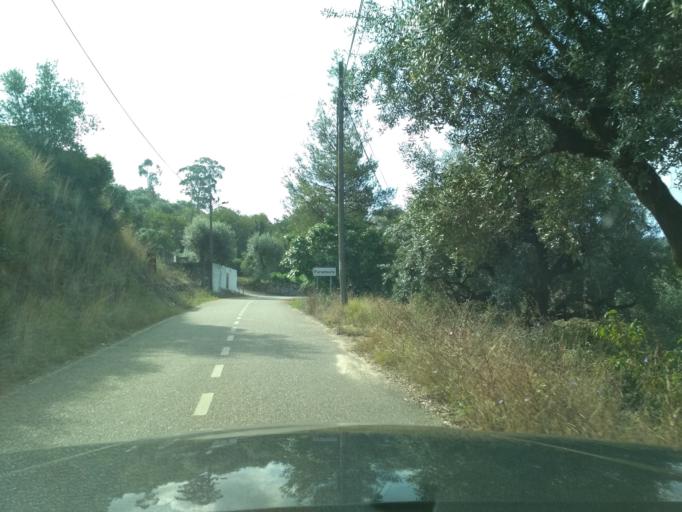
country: PT
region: Coimbra
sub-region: Condeixa-A-Nova
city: Condeixa-a-Nova
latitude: 40.0706
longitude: -8.4979
